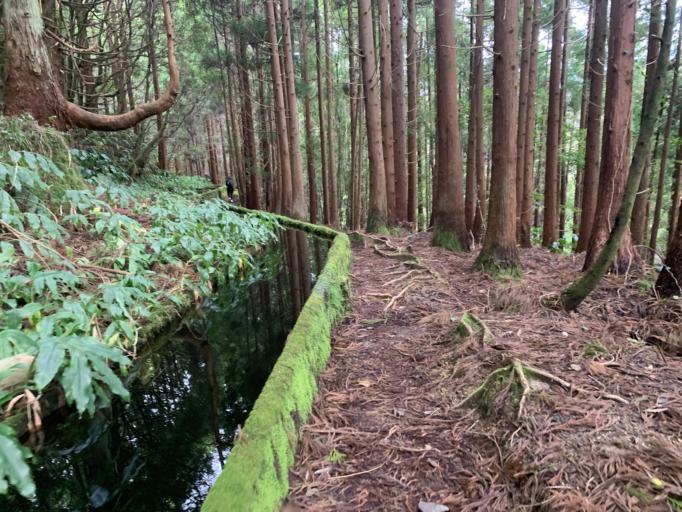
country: PT
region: Azores
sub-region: Vila Franca do Campo
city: Vila Franca do Campo
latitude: 37.7435
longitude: -25.4748
